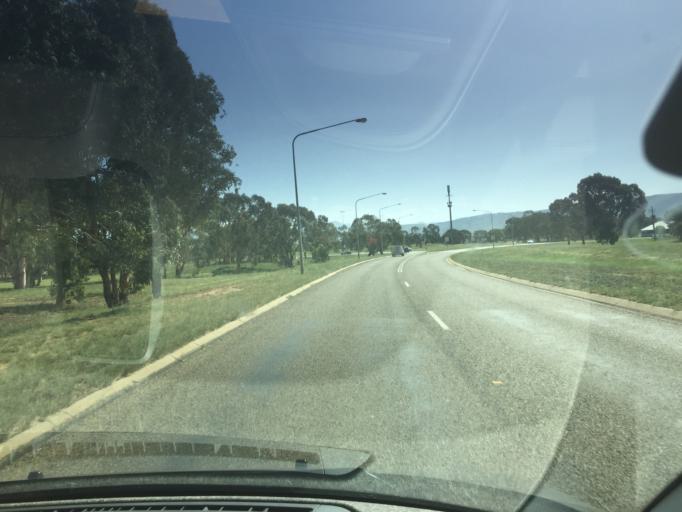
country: AU
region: Australian Capital Territory
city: Macarthur
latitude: -35.4228
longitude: 149.0923
